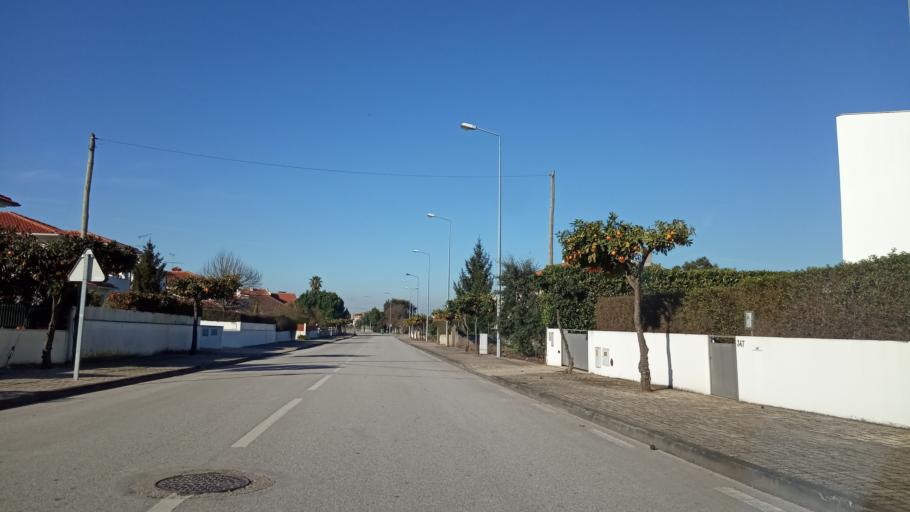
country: PT
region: Aveiro
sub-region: Anadia
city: Anadia
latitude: 40.4296
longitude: -8.4247
